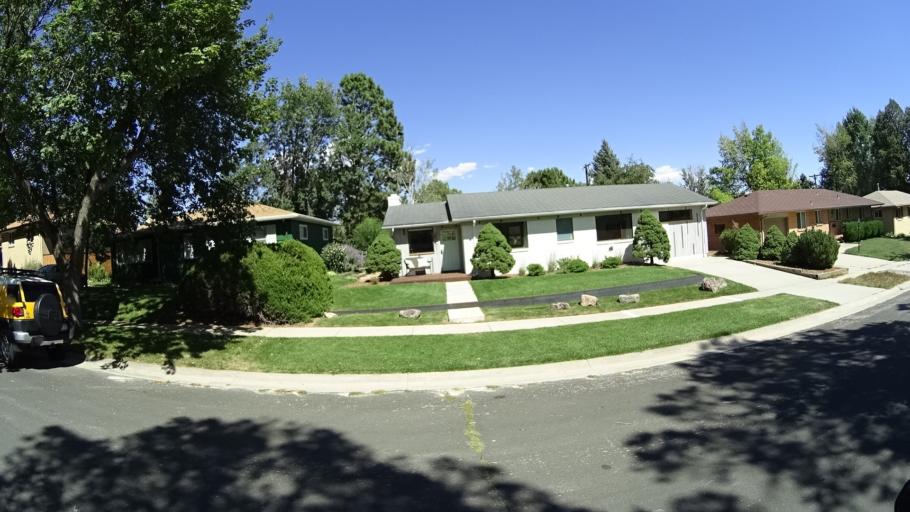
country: US
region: Colorado
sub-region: El Paso County
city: Manitou Springs
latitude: 38.8630
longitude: -104.8717
